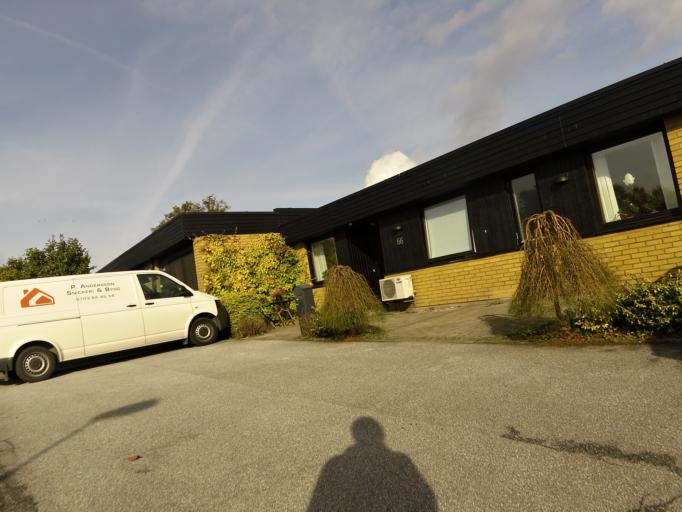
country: SE
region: Skane
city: Bjarred
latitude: 55.7168
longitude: 13.0356
